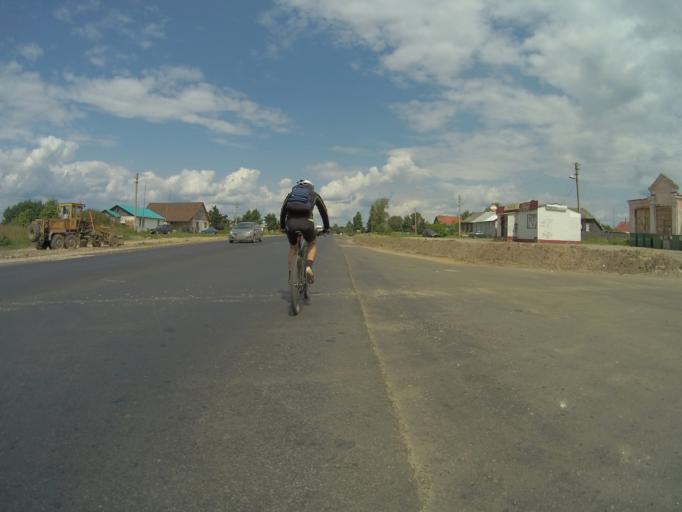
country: RU
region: Vladimir
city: Kideksha
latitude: 56.5150
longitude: 40.5516
